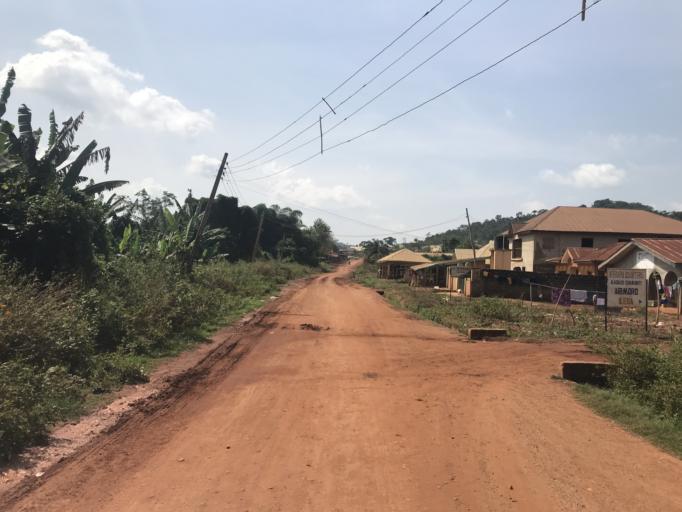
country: NG
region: Osun
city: Ilesa
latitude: 7.6214
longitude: 4.7075
